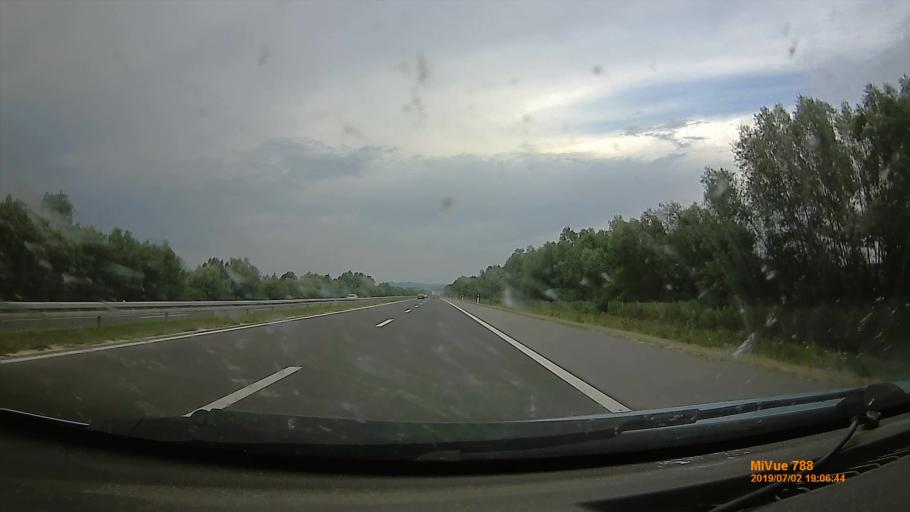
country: HR
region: Varazdinska
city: Remetinec
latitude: 46.0224
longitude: 16.2949
